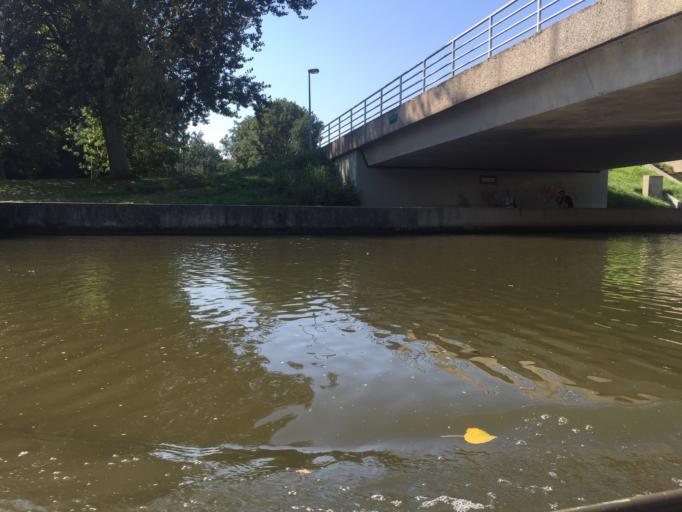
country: NL
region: Flevoland
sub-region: Gemeente Almere
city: Almere Stad
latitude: 52.3807
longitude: 5.1922
